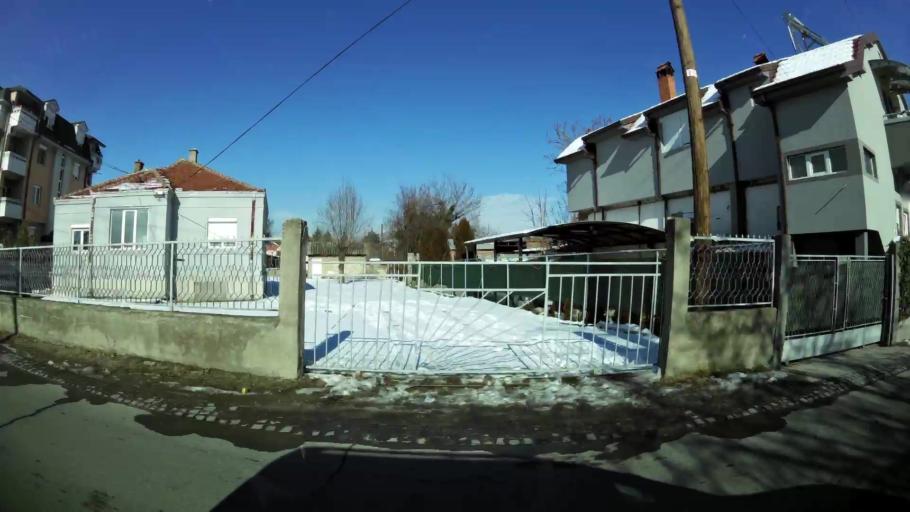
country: MK
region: Saraj
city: Saraj
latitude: 42.0097
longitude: 21.3558
